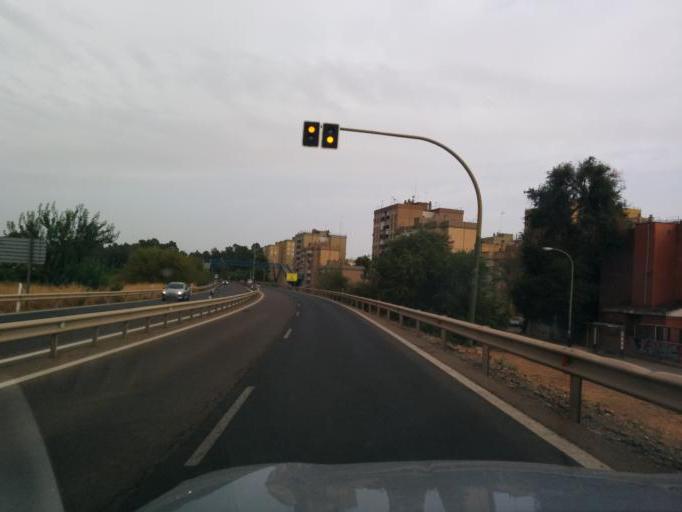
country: ES
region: Andalusia
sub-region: Provincia de Sevilla
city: Sevilla
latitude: 37.4257
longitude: -5.9625
